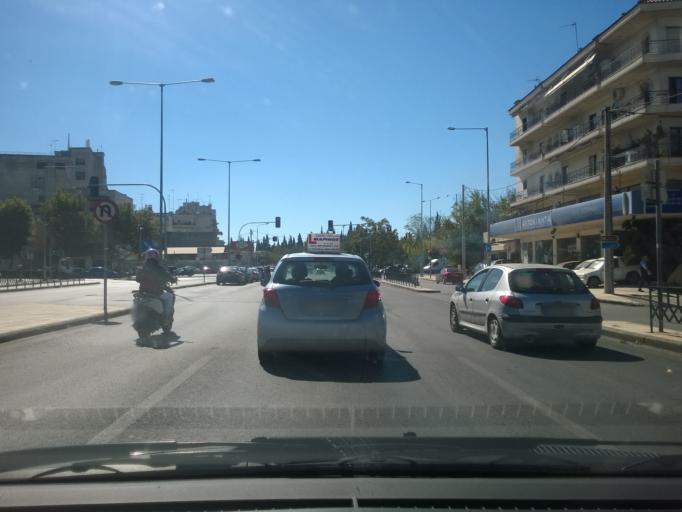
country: GR
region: Central Macedonia
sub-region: Nomos Thessalonikis
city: Ampelokipoi
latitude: 40.6573
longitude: 22.9345
